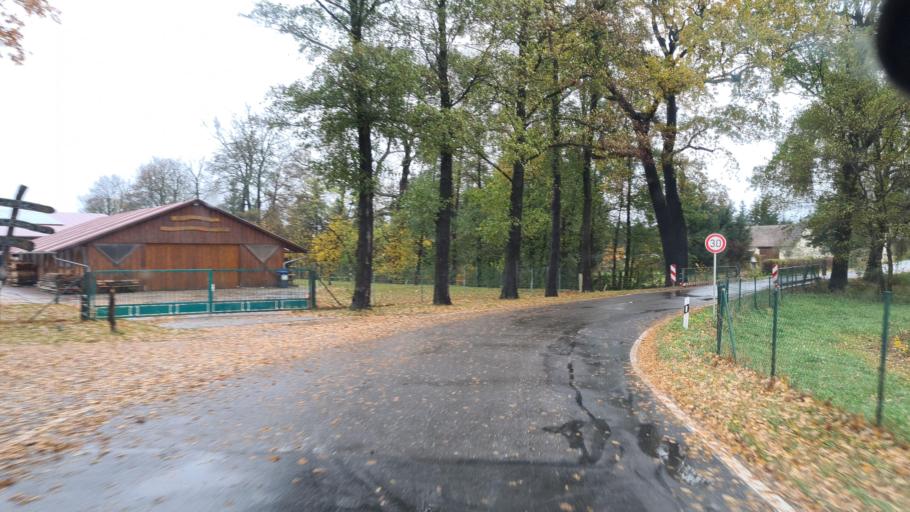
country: DE
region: Brandenburg
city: Drebkau
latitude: 51.6776
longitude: 14.1994
